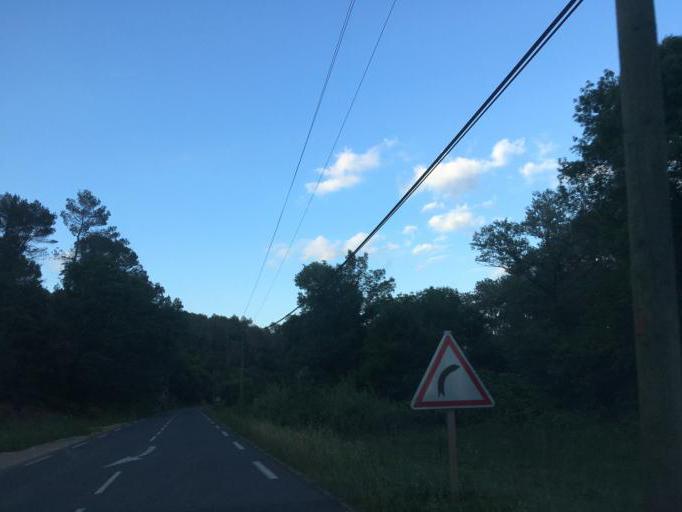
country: FR
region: Provence-Alpes-Cote d'Azur
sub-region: Departement du Var
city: Carces
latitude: 43.4811
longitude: 6.2015
